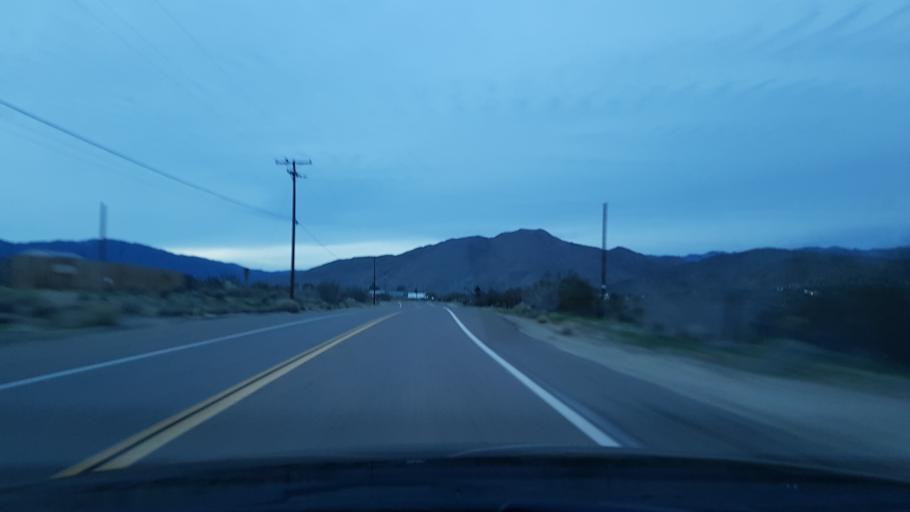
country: US
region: California
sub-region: San Diego County
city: Julian
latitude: 33.0733
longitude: -116.4340
